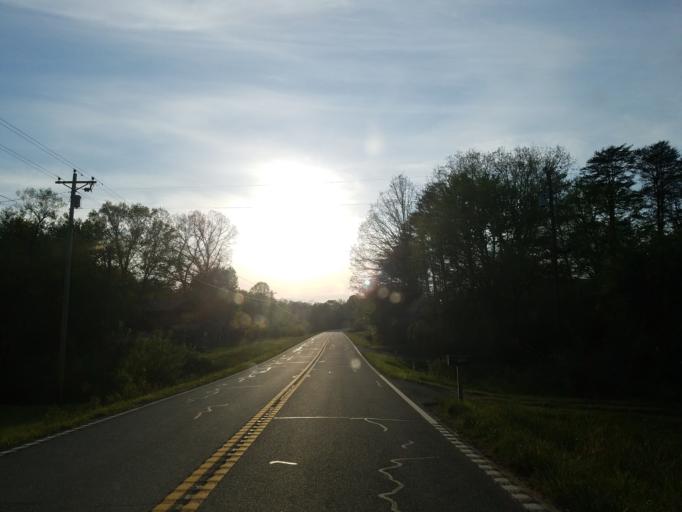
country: US
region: Georgia
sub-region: Fannin County
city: Blue Ridge
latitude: 34.8457
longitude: -84.2132
